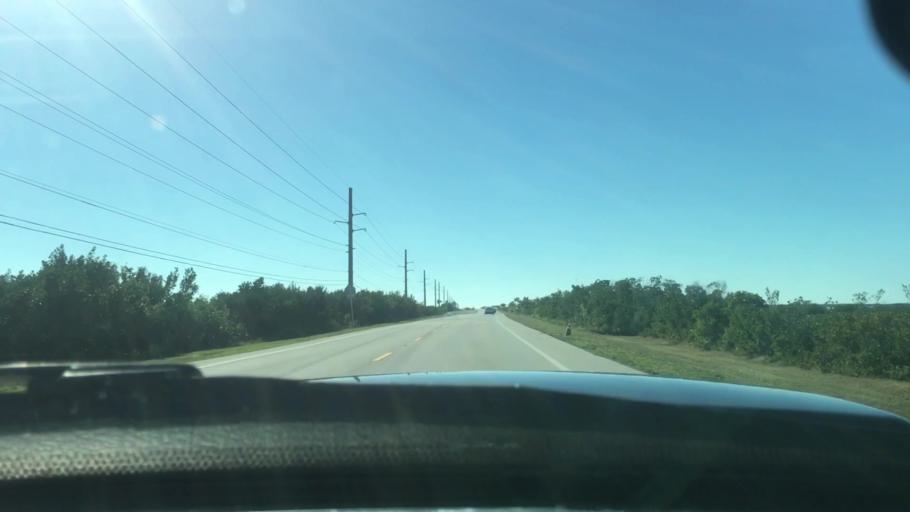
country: US
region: Florida
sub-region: Monroe County
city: Cudjoe Key
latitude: 24.6564
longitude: -81.5346
